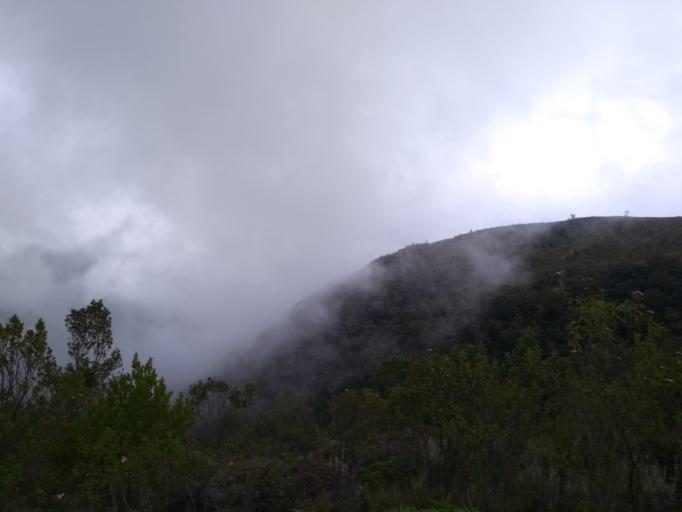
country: CO
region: Cesar
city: Manaure Balcon del Cesar
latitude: 10.2138
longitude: -73.0108
